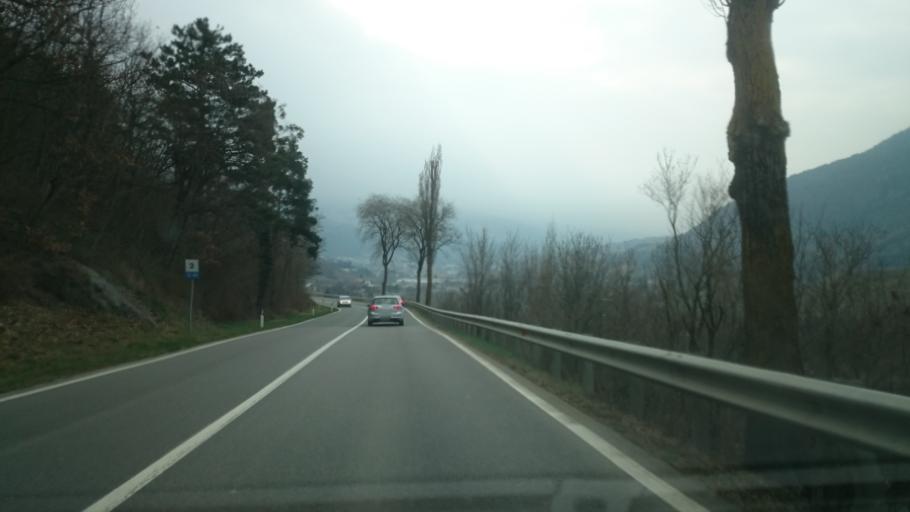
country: IT
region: Trentino-Alto Adige
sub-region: Bolzano
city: Varna
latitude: 46.7487
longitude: 11.6474
